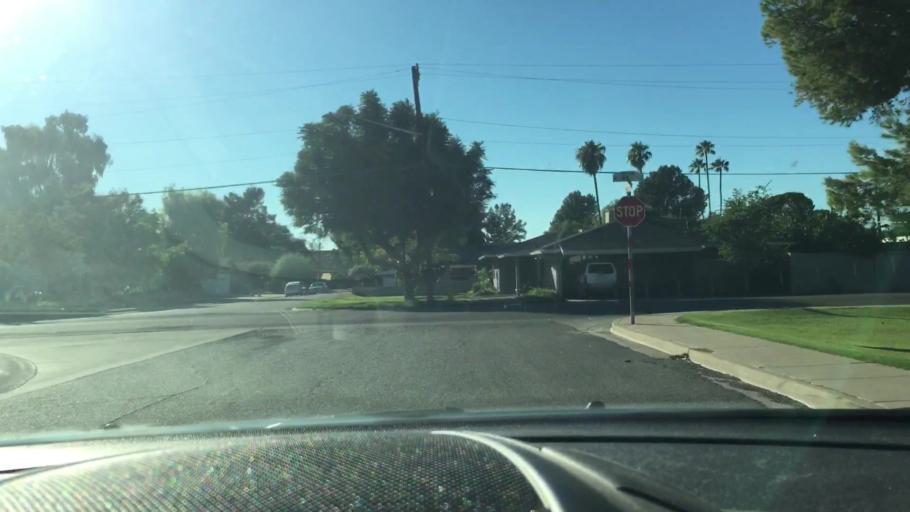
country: US
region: Arizona
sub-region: Maricopa County
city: Paradise Valley
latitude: 33.4835
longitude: -111.9823
